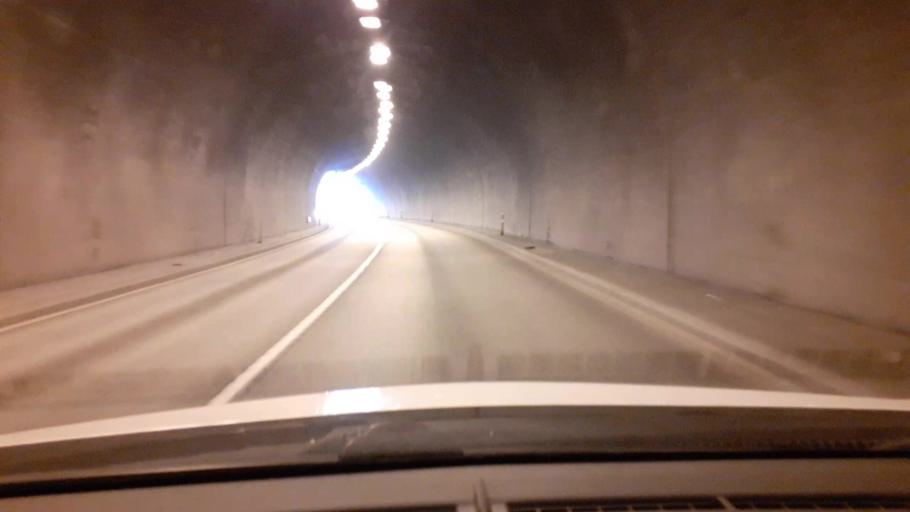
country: IS
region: Capital Region
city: Reykjavik
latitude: 64.2829
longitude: -21.8413
